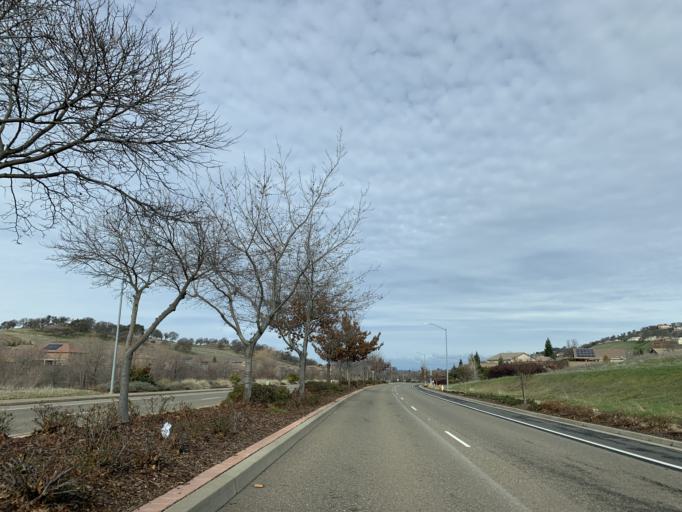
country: US
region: California
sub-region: El Dorado County
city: El Dorado Hills
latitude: 38.6596
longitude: -121.0945
